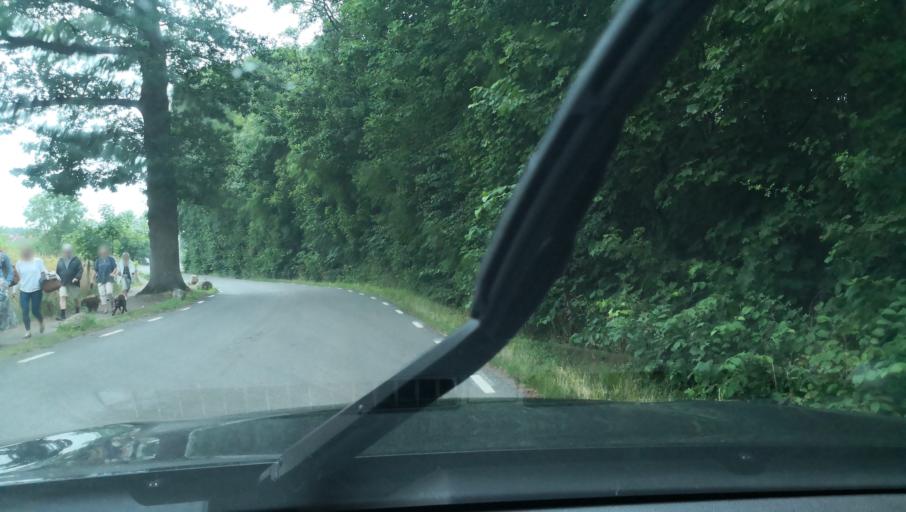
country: SE
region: Skane
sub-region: Simrishamns Kommun
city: Kivik
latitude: 55.6827
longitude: 14.2351
